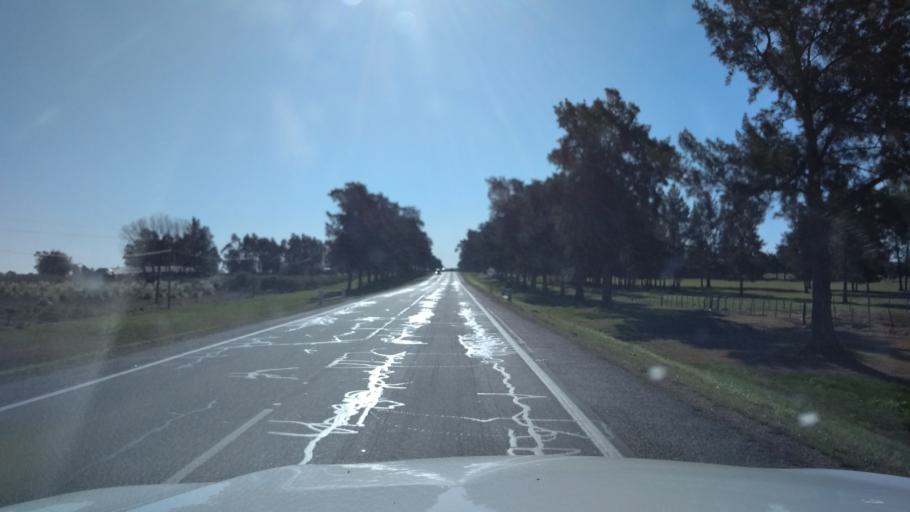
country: UY
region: Canelones
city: San Jacinto
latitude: -34.5806
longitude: -55.8442
